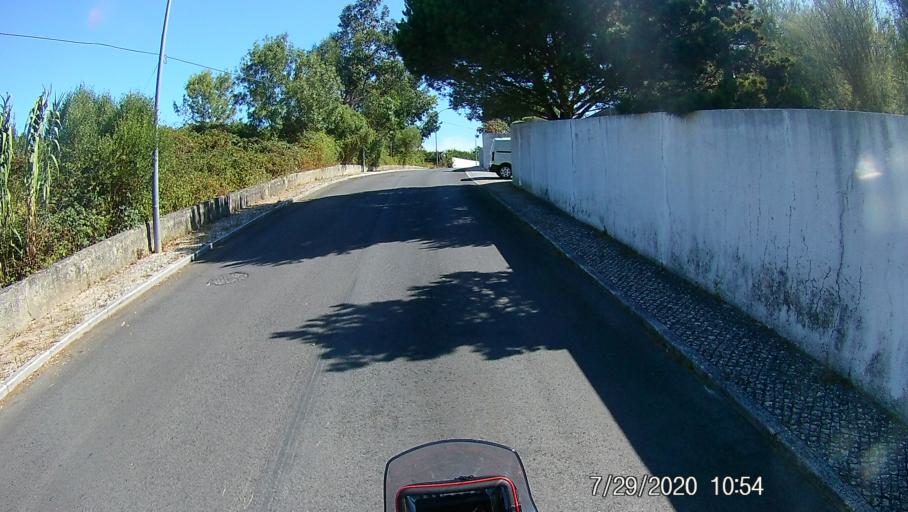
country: PT
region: Lisbon
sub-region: Sintra
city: Rio de Mouro
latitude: 38.7531
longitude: -9.3655
